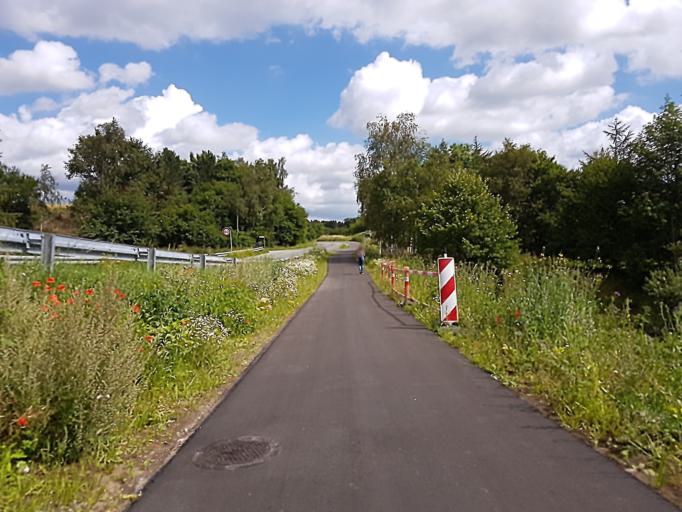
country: DK
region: Capital Region
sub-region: Egedal Kommune
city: Ganlose
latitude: 55.8003
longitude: 12.2781
